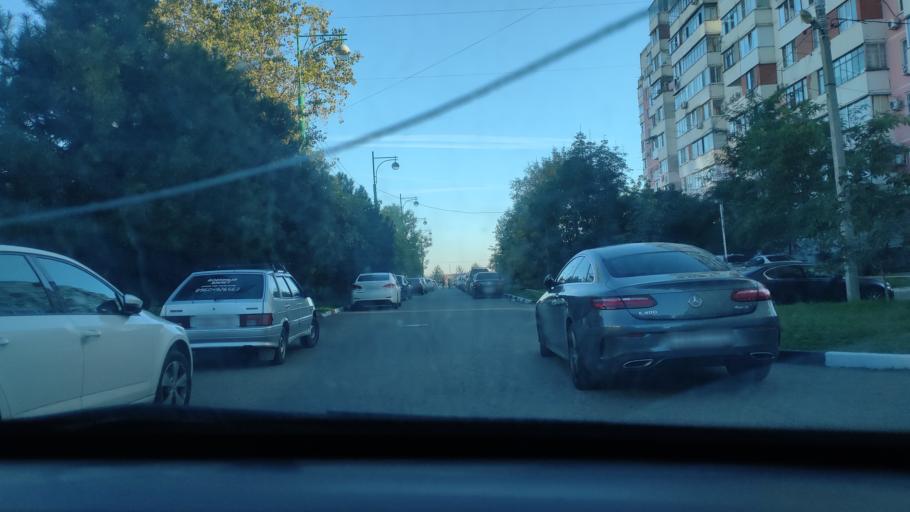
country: RU
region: Adygeya
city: Yablonovskiy
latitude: 45.0284
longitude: 38.9124
